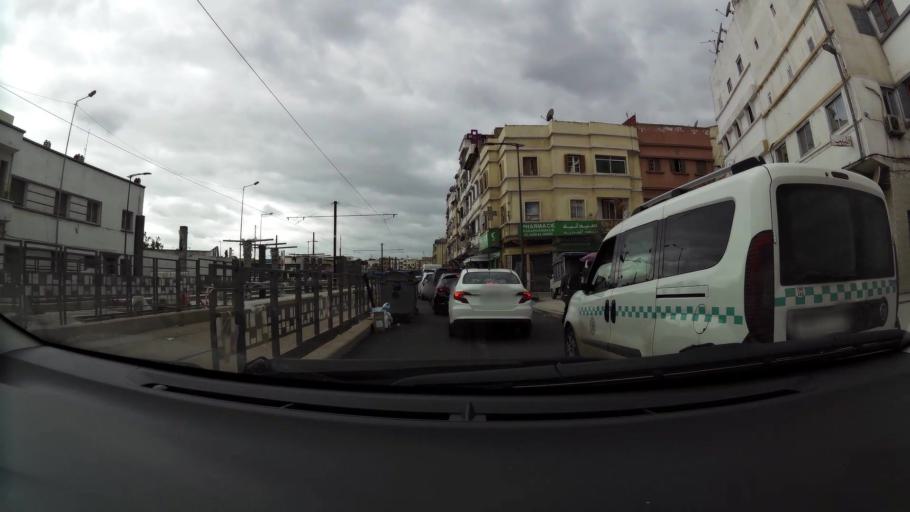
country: MA
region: Grand Casablanca
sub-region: Casablanca
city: Casablanca
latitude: 33.5816
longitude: -7.5629
